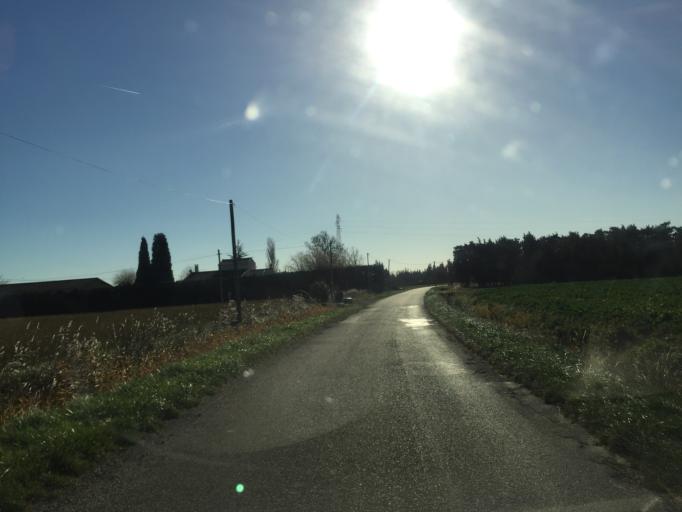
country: FR
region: Provence-Alpes-Cote d'Azur
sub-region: Departement du Vaucluse
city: Bedarrides
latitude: 44.0597
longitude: 4.9076
